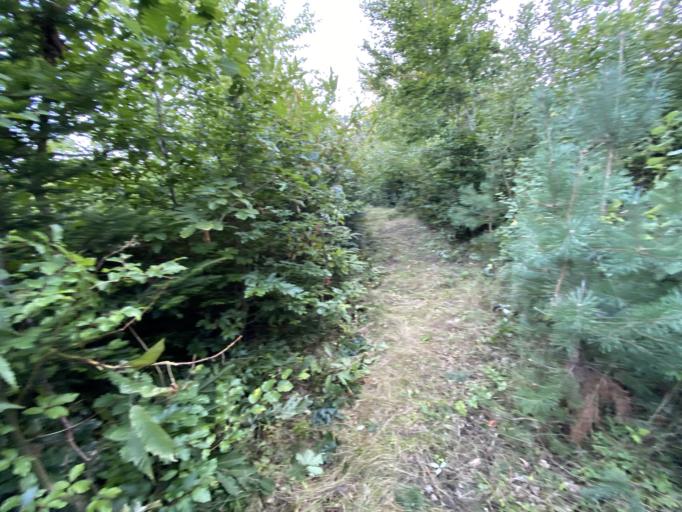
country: AT
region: Burgenland
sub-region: Politischer Bezirk Oberpullendorf
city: Kobersdorf
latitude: 47.5849
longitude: 16.3790
